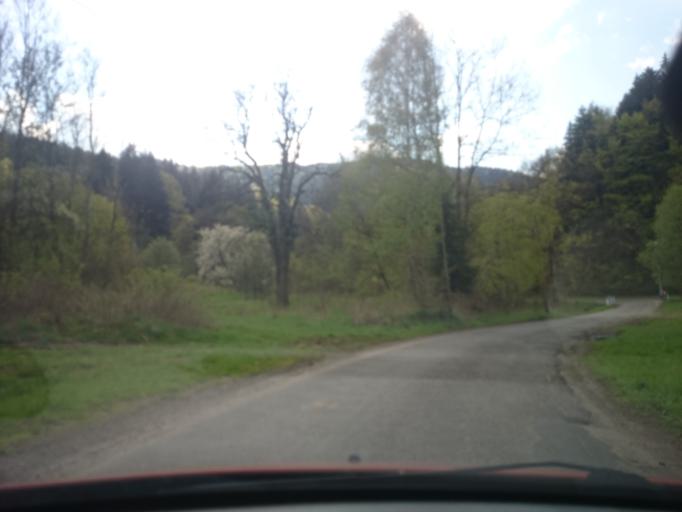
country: PL
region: Lower Silesian Voivodeship
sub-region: Powiat klodzki
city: Bystrzyca Klodzka
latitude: 50.2974
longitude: 16.5512
